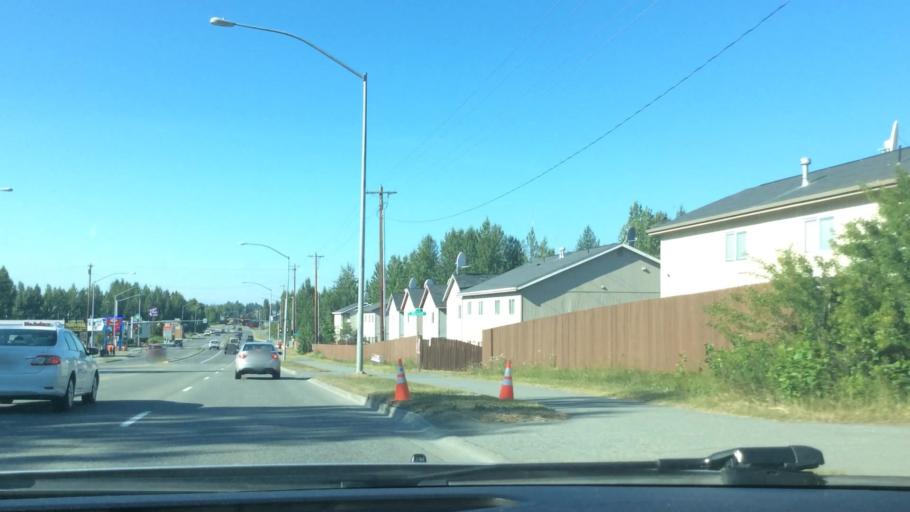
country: US
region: Alaska
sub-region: Anchorage Municipality
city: Anchorage
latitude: 61.1572
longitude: -149.8341
